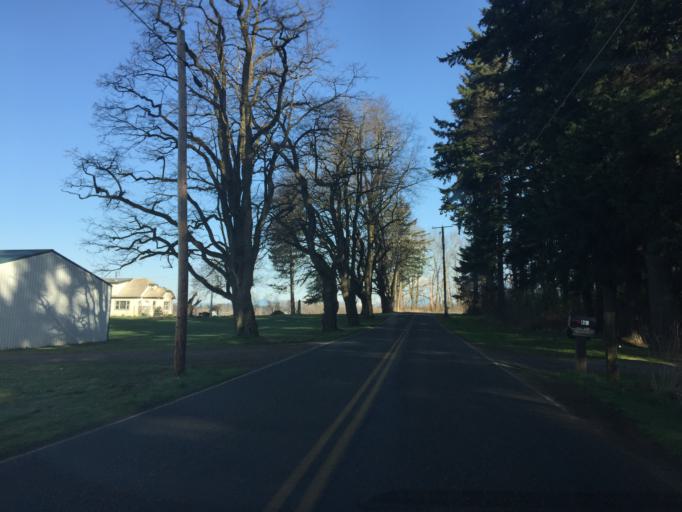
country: US
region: Washington
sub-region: Whatcom County
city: Lynden
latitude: 48.9045
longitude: -122.5132
